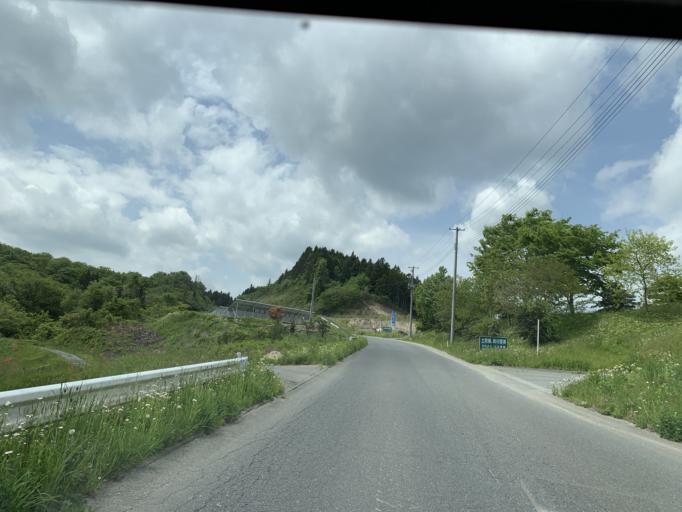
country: JP
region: Miyagi
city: Furukawa
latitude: 38.7238
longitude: 140.9248
